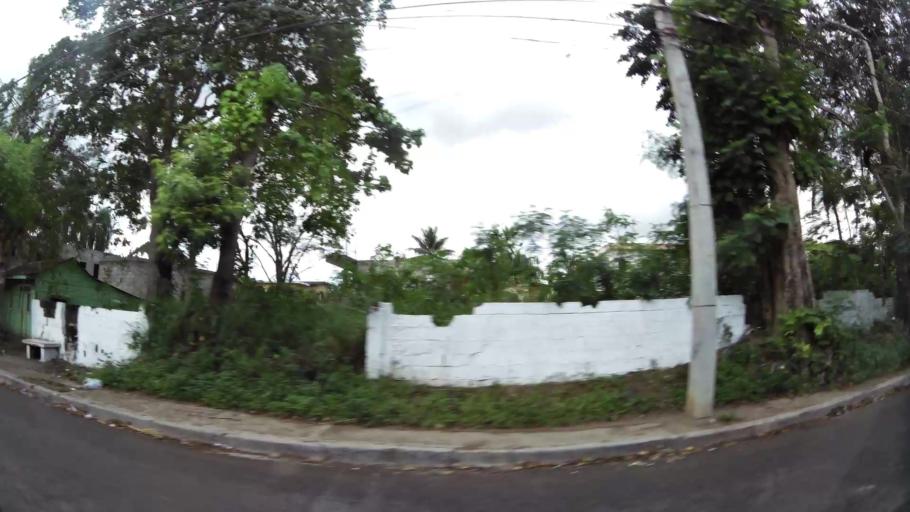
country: DO
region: Nacional
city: La Agustina
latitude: 18.5093
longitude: -69.9528
